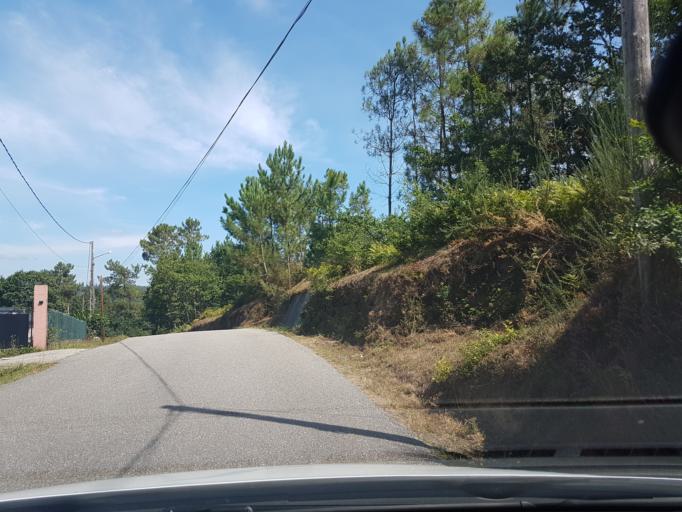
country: ES
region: Galicia
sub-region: Provincia de Pontevedra
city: Porrino
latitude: 42.1959
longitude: -8.6220
